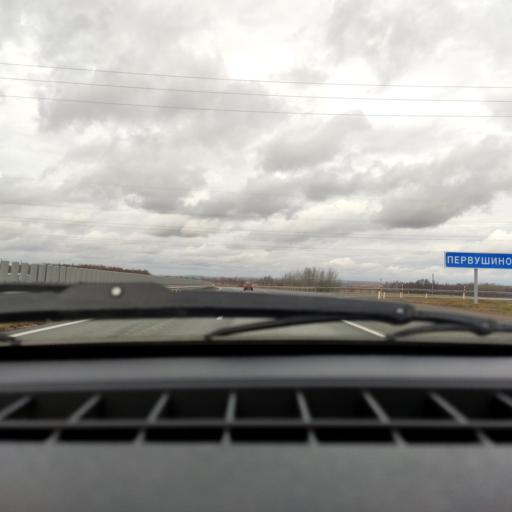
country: RU
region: Bashkortostan
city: Asanovo
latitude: 54.9607
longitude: 55.5853
